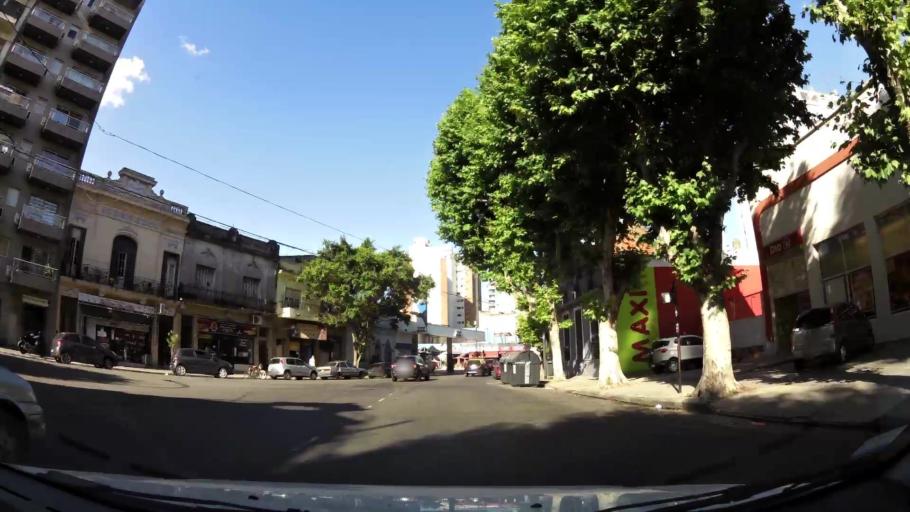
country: AR
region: Buenos Aires F.D.
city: Villa Santa Rita
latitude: -34.6161
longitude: -58.4426
